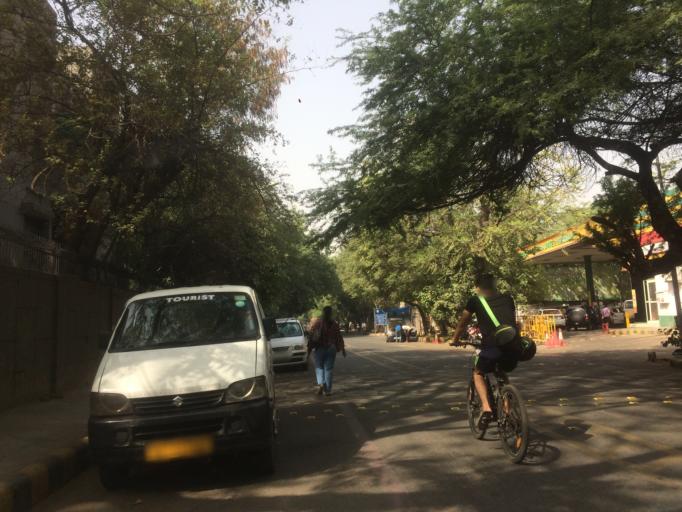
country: IN
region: NCT
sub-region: New Delhi
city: New Delhi
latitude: 28.6332
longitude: 77.2020
